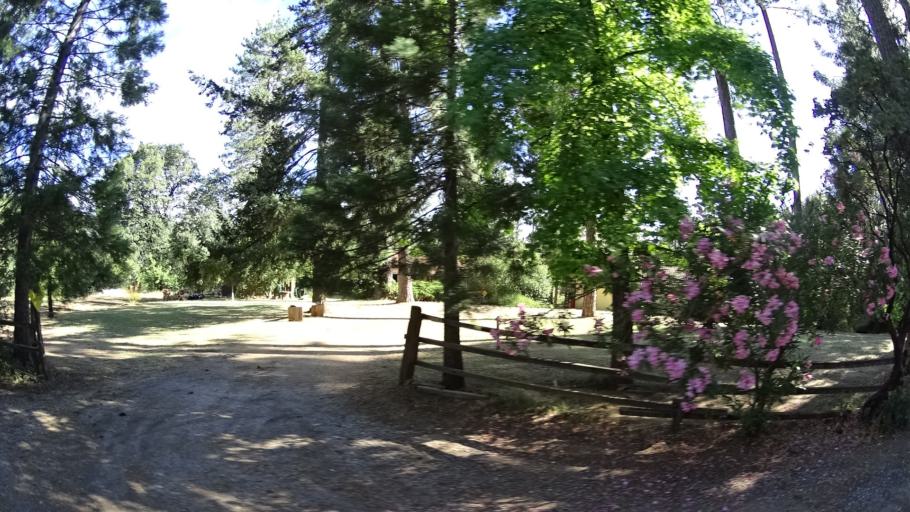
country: US
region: California
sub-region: Amador County
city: Pioneer
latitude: 38.3853
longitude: -120.5576
